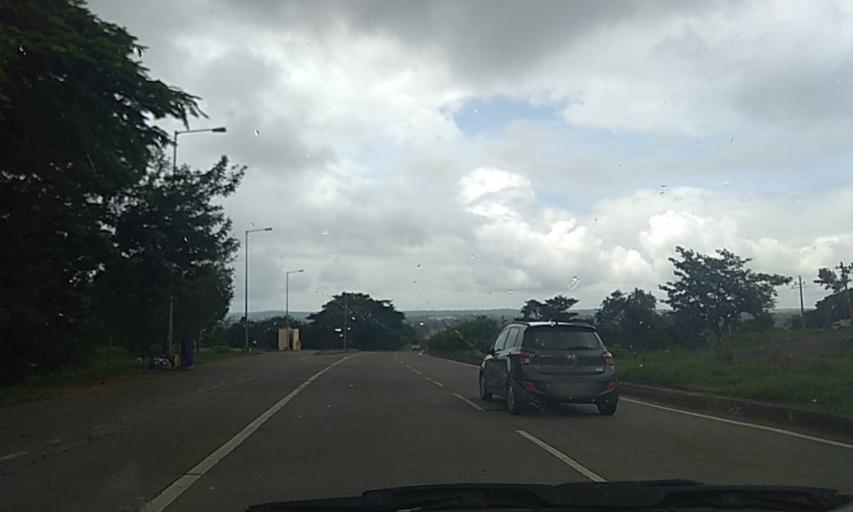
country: IN
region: Karnataka
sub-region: Belgaum
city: Sankeshwar
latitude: 16.2887
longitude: 74.4426
